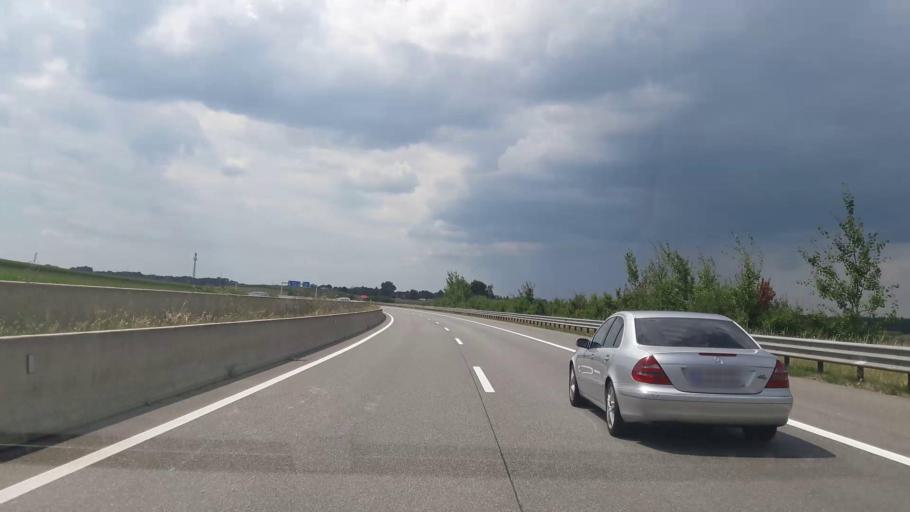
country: AT
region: Upper Austria
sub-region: Politischer Bezirk Vocklabruck
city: Aurach am Hongar
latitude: 47.9553
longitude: 13.6512
